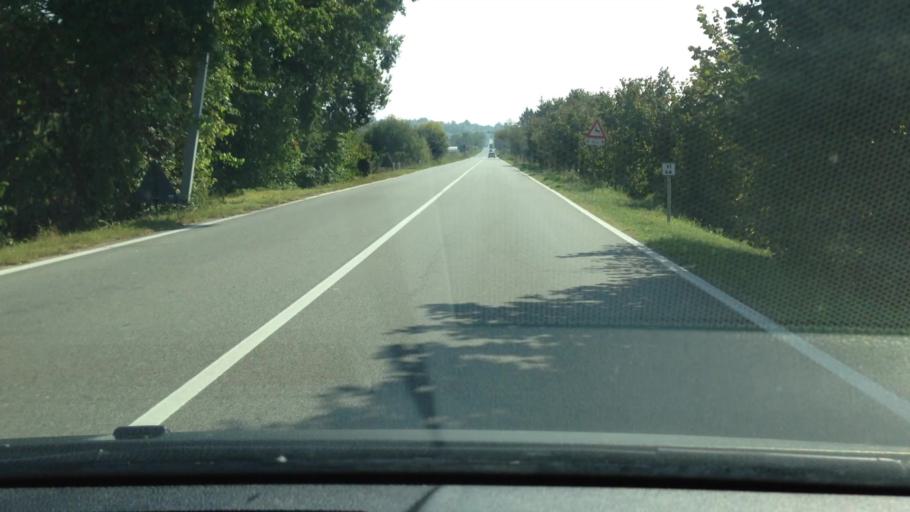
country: IT
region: Piedmont
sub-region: Provincia di Asti
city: Rocca d'Arazzo
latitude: 44.9055
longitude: 8.2858
